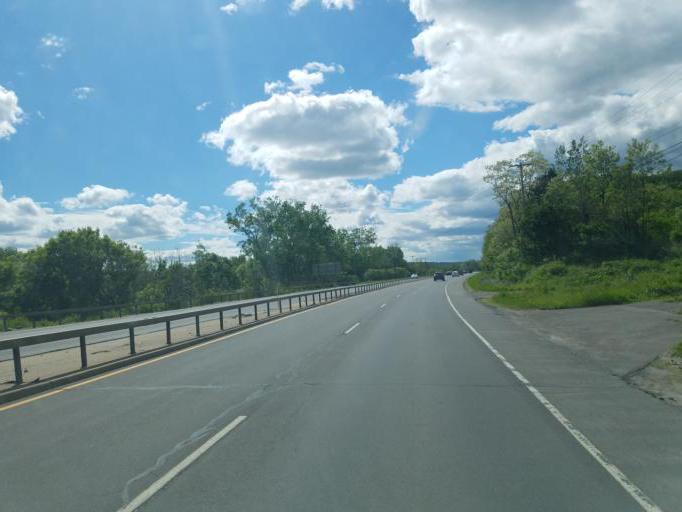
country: US
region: New York
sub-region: Herkimer County
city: Mohawk
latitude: 43.0175
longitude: -75.0162
